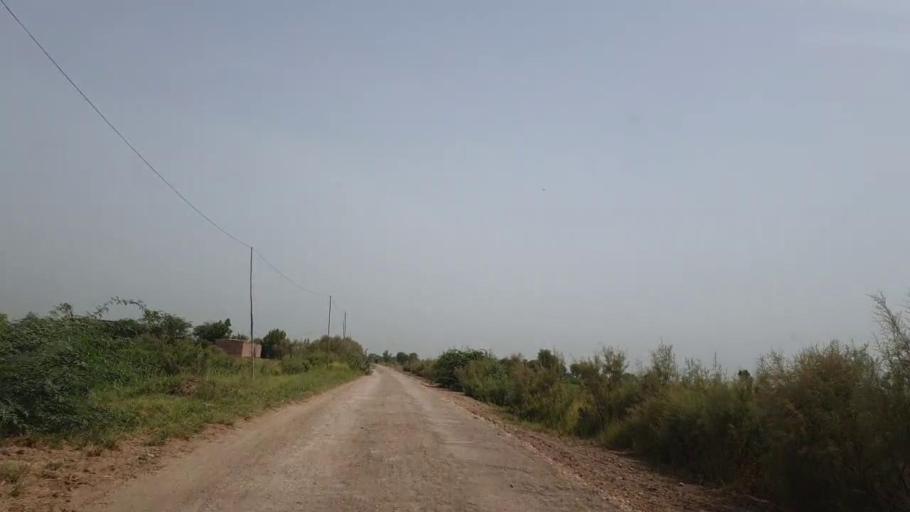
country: PK
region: Sindh
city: Sakrand
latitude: 26.1251
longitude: 68.3690
